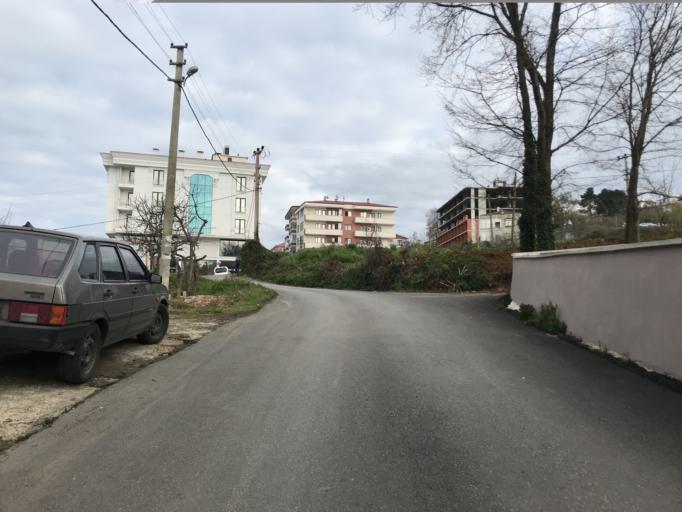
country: TR
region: Trabzon
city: Trabzon
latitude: 40.9902
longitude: 39.7777
